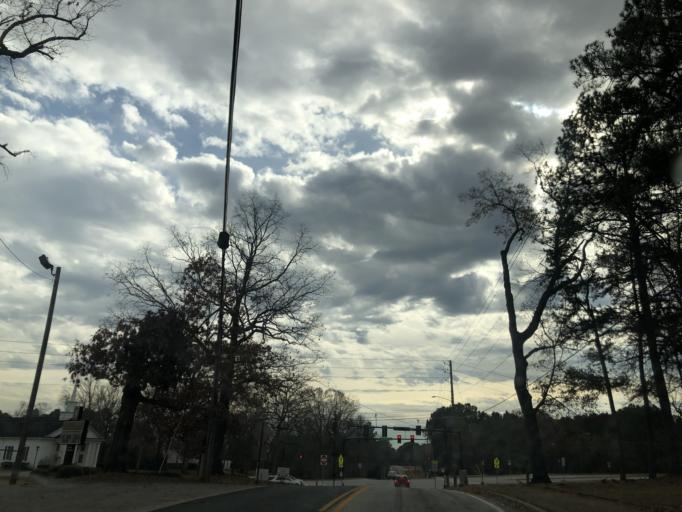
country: US
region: Georgia
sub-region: DeKalb County
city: Panthersville
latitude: 33.6836
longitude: -84.2150
